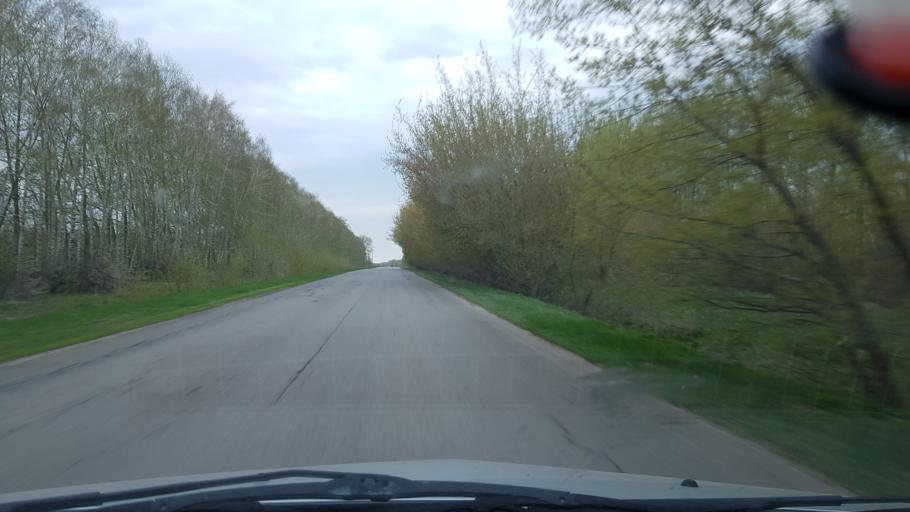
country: RU
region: Samara
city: Podstepki
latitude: 53.6650
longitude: 49.1745
